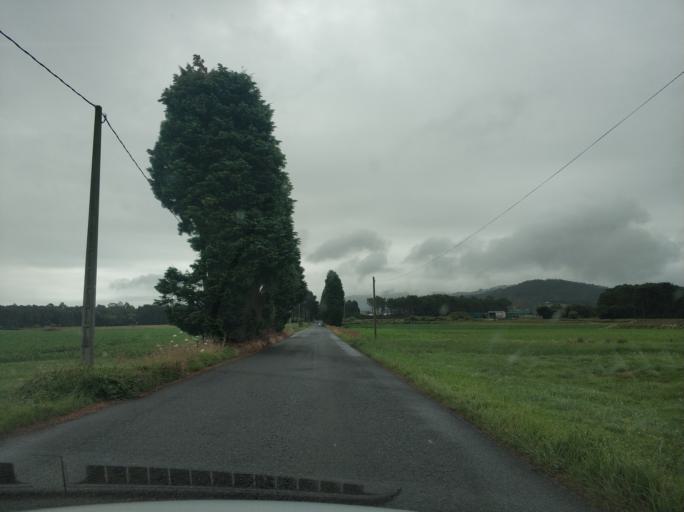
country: ES
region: Asturias
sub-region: Province of Asturias
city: Tineo
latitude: 43.5529
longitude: -6.4588
